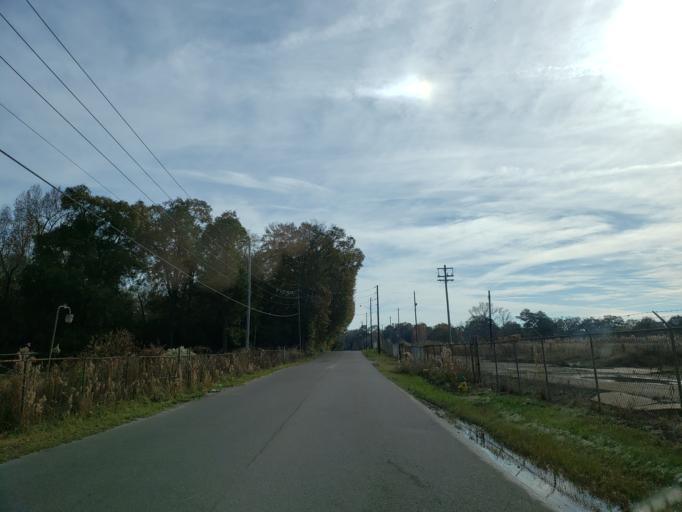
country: US
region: Mississippi
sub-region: Forrest County
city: Hattiesburg
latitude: 31.3388
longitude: -89.3043
